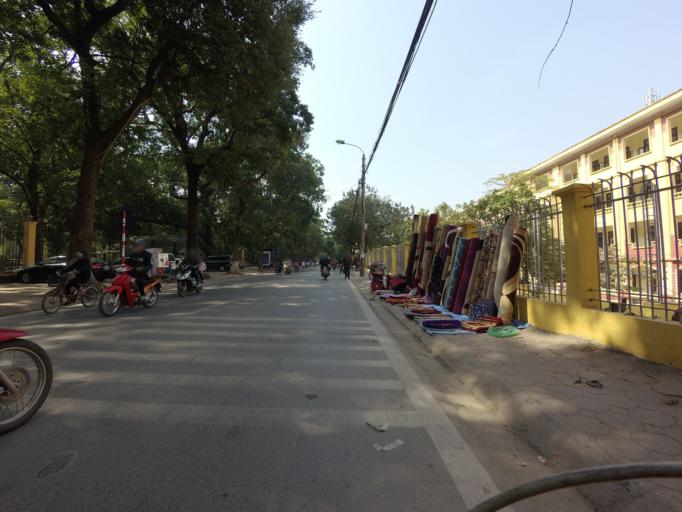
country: VN
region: Ha Noi
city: Hanoi
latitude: 21.0420
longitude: 105.8334
